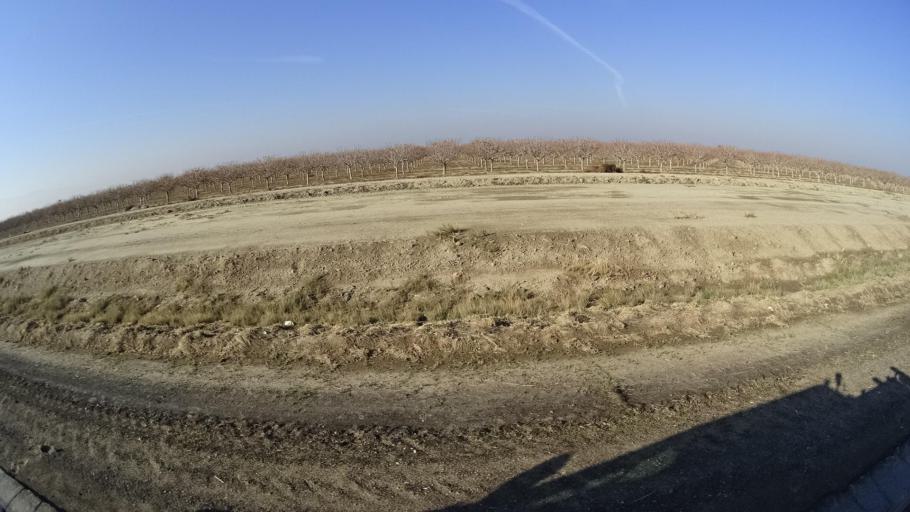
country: US
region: California
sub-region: Kern County
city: Weedpatch
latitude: 35.2040
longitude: -118.9677
